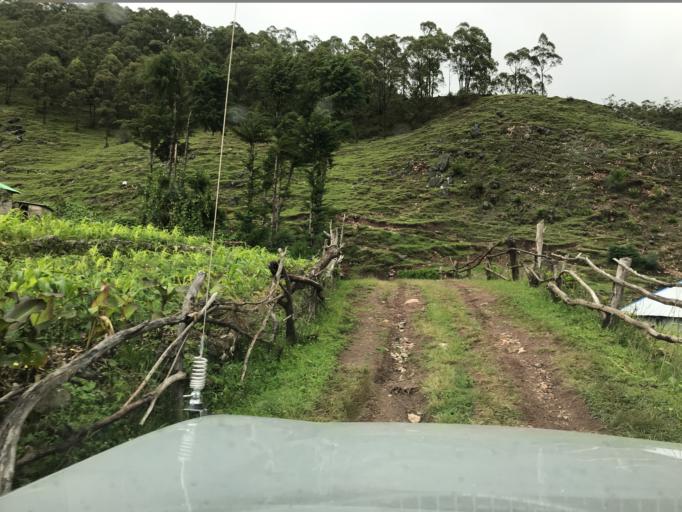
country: TL
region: Ainaro
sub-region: Ainaro
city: Ainaro
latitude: -8.8723
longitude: 125.5509
